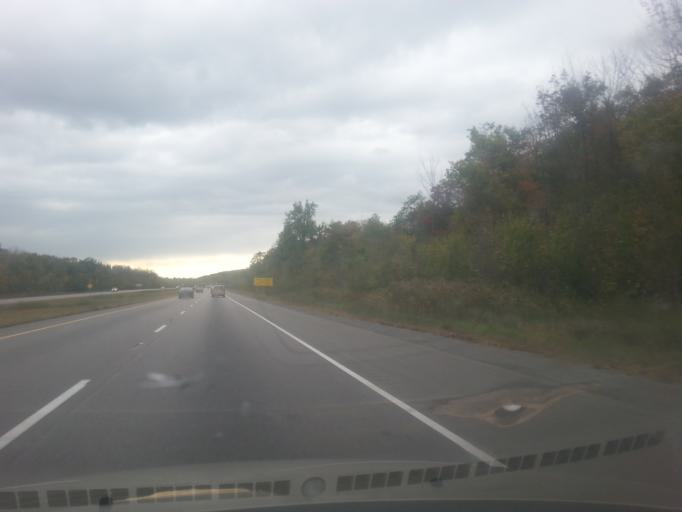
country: CA
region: Ontario
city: Quinte West
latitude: 44.1064
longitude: -77.6710
